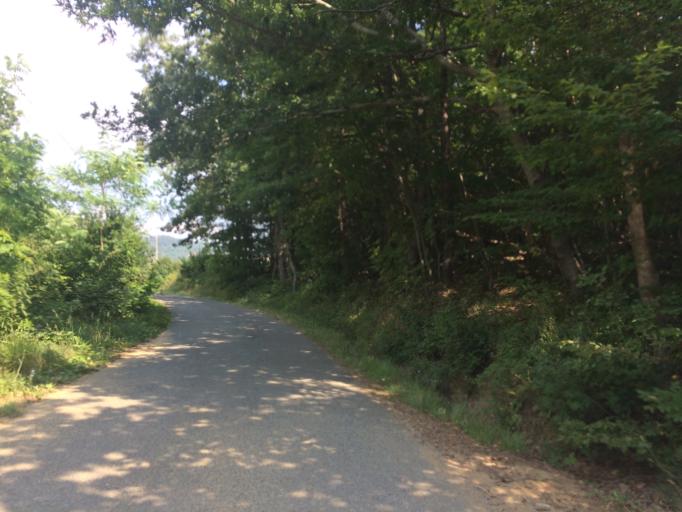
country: IT
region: Liguria
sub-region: Provincia di Savona
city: Molino-Pera
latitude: 44.4805
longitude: 8.3535
